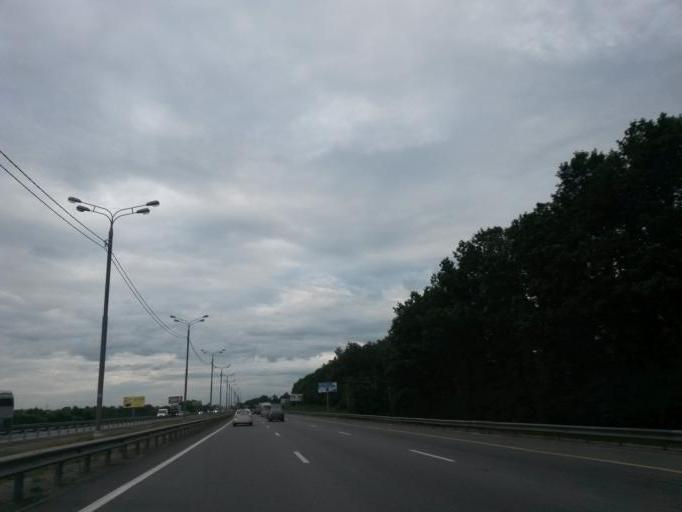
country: RU
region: Moskovskaya
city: Vidnoye
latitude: 55.5319
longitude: 37.6996
